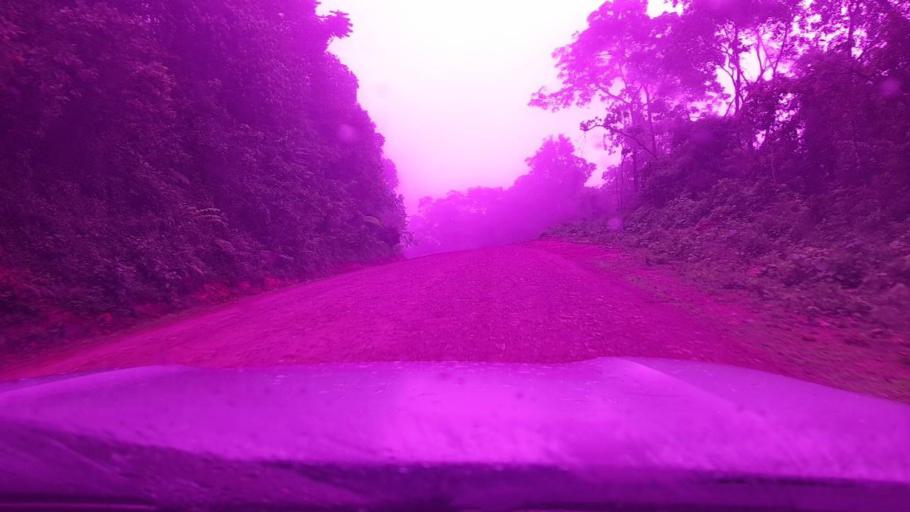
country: ET
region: Southern Nations, Nationalities, and People's Region
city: Bonga
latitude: 7.5138
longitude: 36.0573
